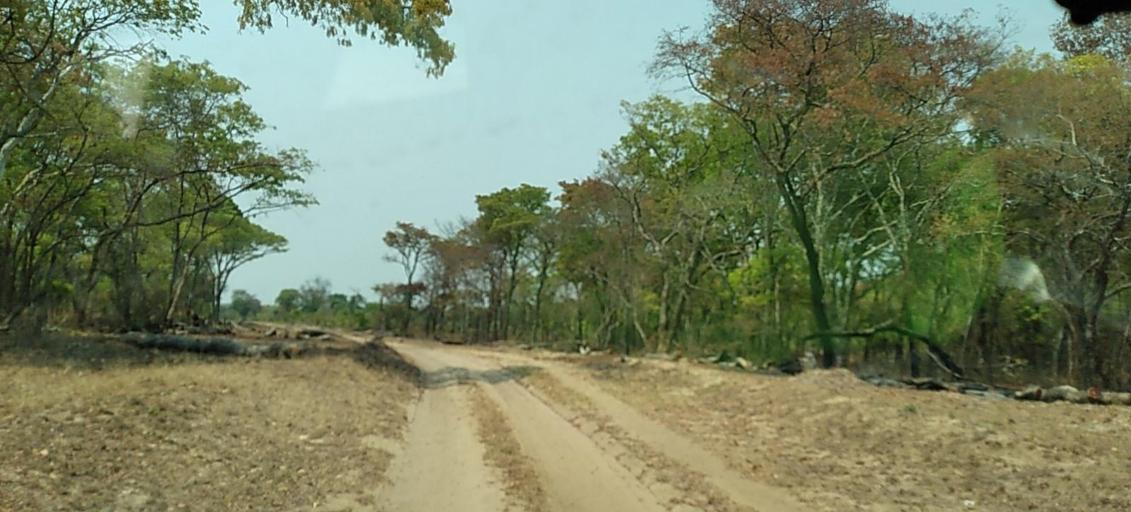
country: ZM
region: Western
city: Lukulu
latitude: -13.9595
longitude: 23.2247
